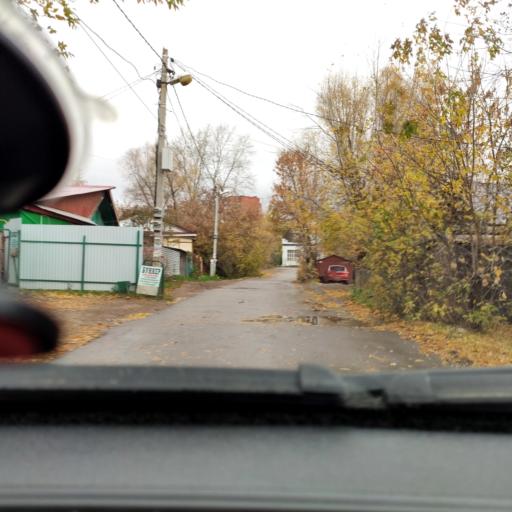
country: RU
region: Bashkortostan
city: Ufa
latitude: 54.7416
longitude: 56.0010
